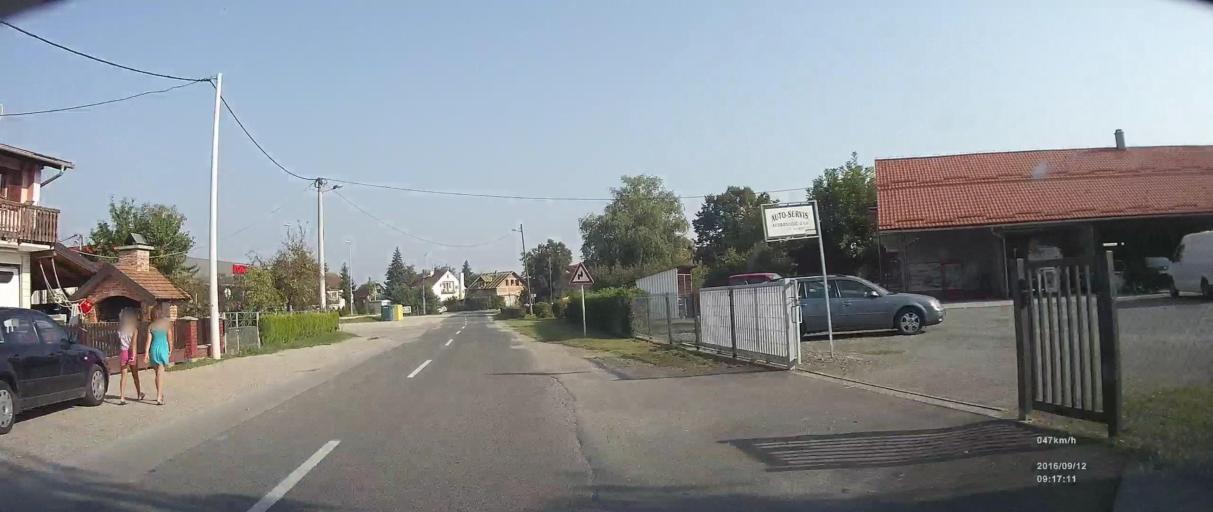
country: HR
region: Zagrebacka
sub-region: Grad Velika Gorica
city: Velika Gorica
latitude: 45.7028
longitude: 16.0669
